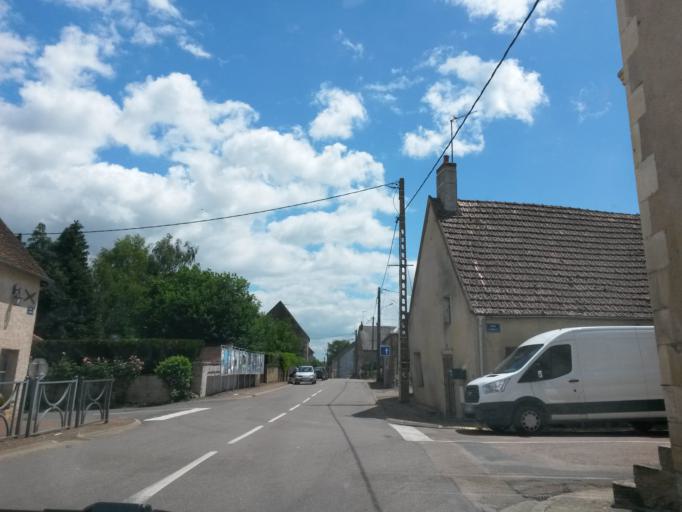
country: FR
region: Bourgogne
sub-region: Departement de la Nievre
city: Pouilly-sur-Loire
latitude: 47.3429
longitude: 2.9904
